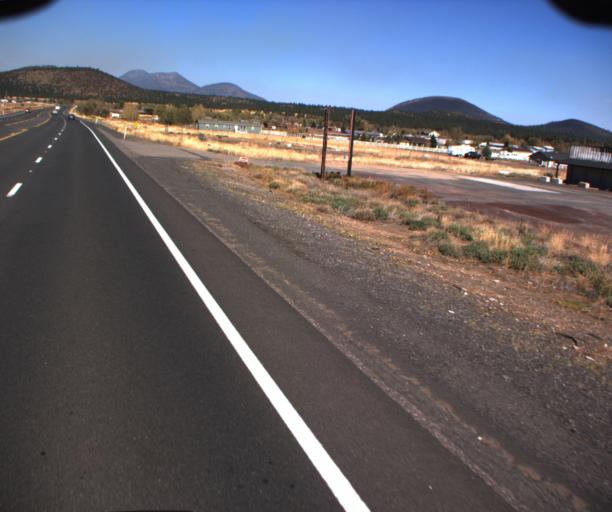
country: US
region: Arizona
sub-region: Coconino County
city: Flagstaff
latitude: 35.3124
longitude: -111.5426
